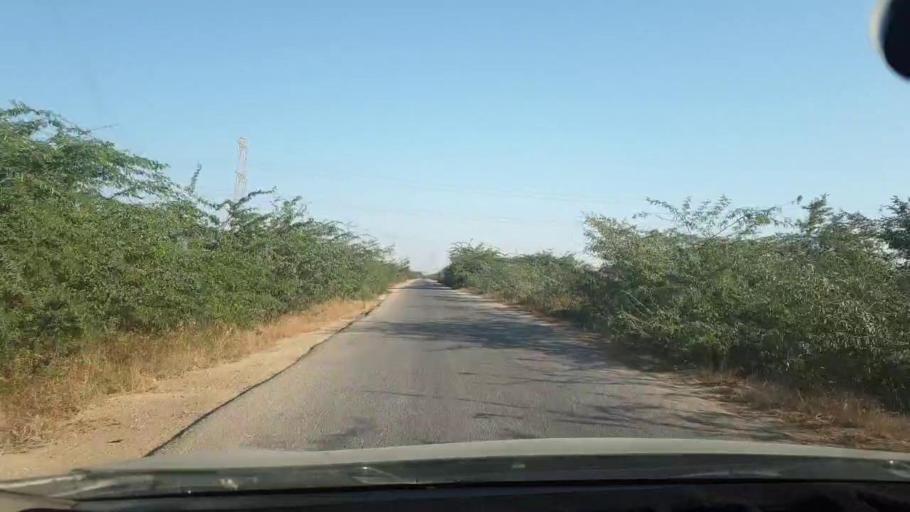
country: PK
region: Sindh
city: Malir Cantonment
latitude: 25.1594
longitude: 67.1937
